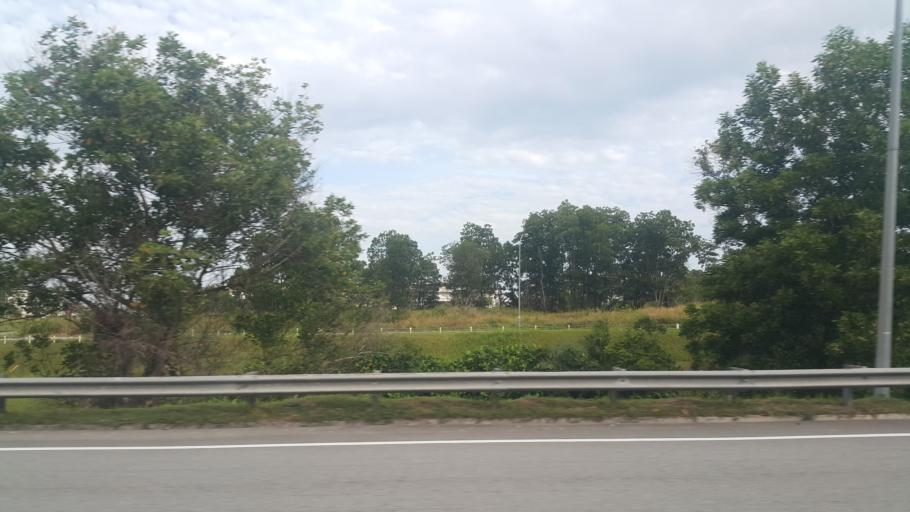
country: MY
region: Johor
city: Skudai
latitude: 1.4362
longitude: 103.6081
